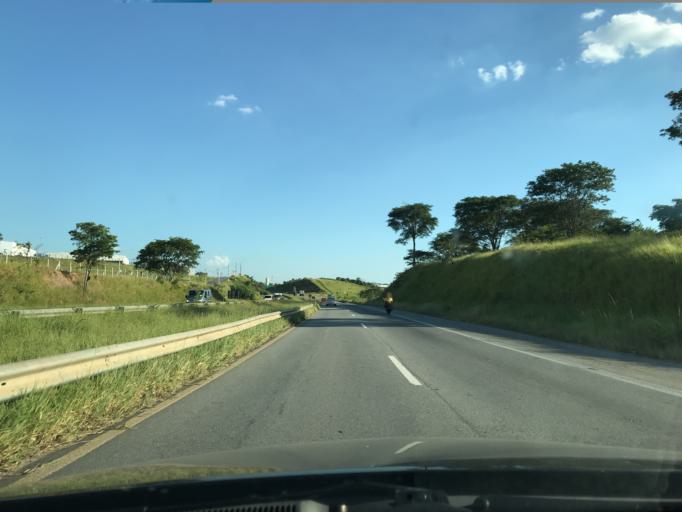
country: BR
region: Sao Paulo
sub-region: Taubate
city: Taubate
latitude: -23.0450
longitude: -45.6276
